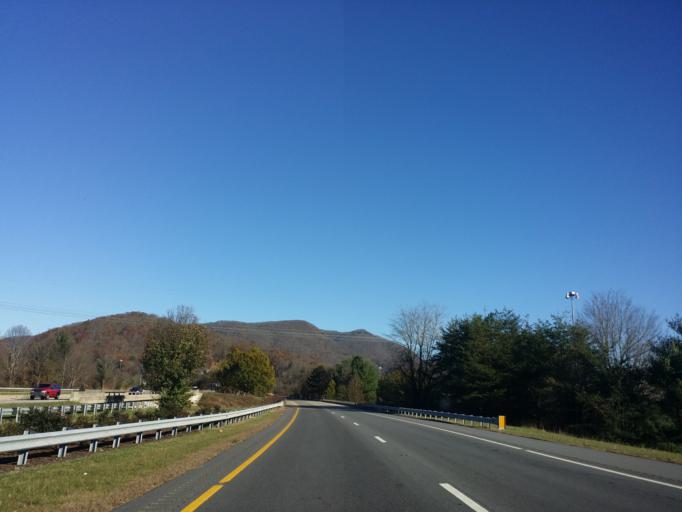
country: US
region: North Carolina
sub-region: Buncombe County
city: Biltmore Forest
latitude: 35.5670
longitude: -82.5042
